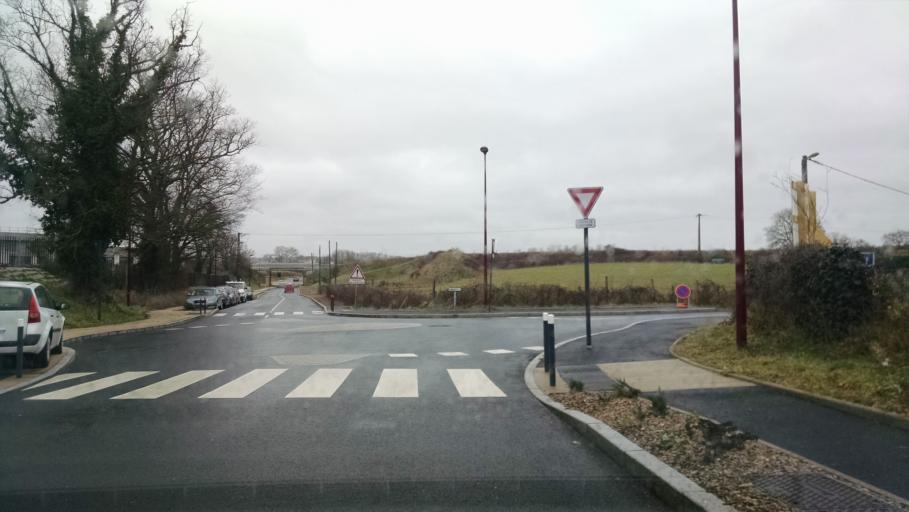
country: FR
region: Pays de la Loire
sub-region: Departement de la Loire-Atlantique
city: Clisson
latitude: 47.0925
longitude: -1.2681
